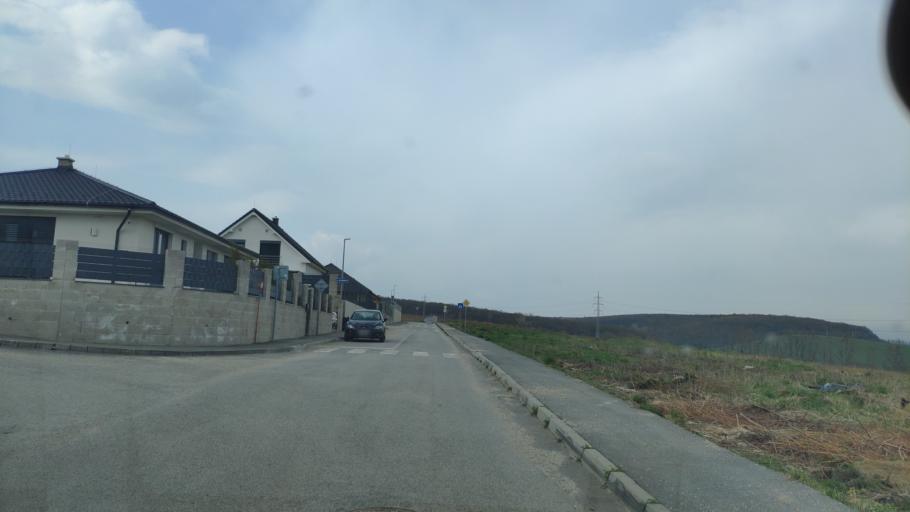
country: SK
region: Kosicky
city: Kosice
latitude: 48.6819
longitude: 21.3099
